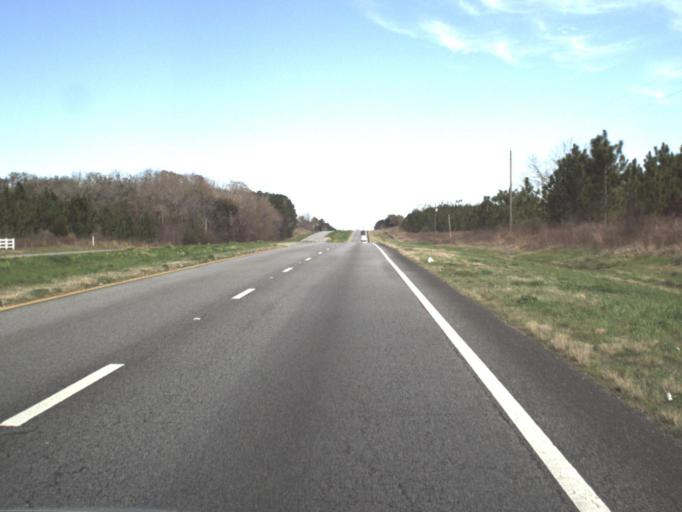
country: US
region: Florida
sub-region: Jackson County
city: Marianna
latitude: 30.8219
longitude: -85.3644
